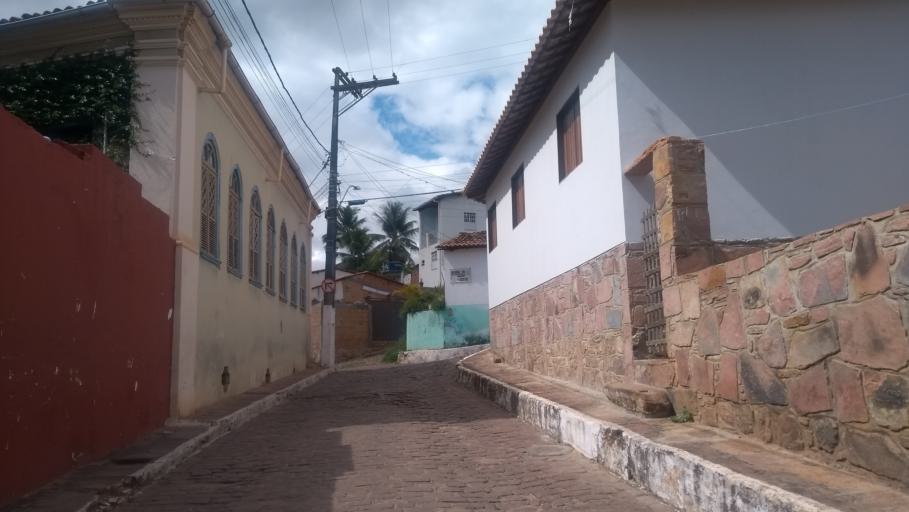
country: BR
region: Bahia
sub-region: Andarai
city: Vera Cruz
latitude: -12.5643
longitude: -41.3894
